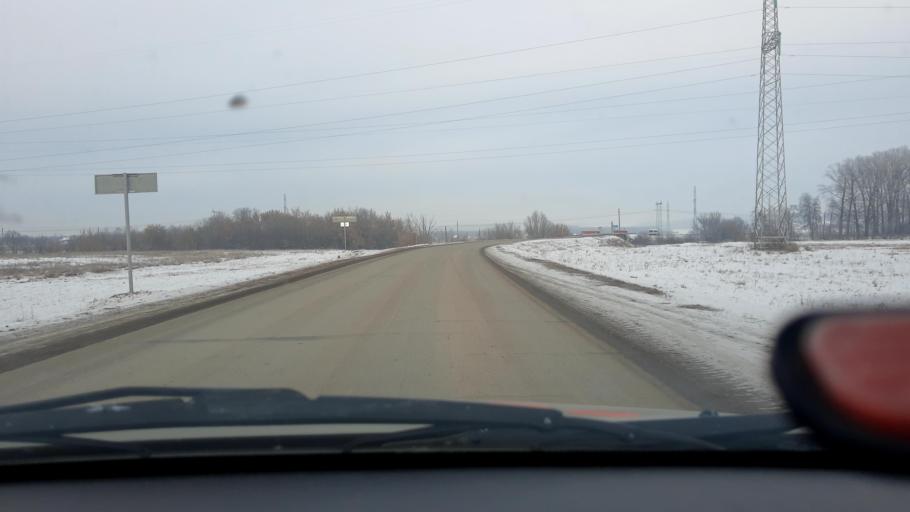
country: RU
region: Bashkortostan
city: Avdon
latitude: 54.4302
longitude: 55.8157
